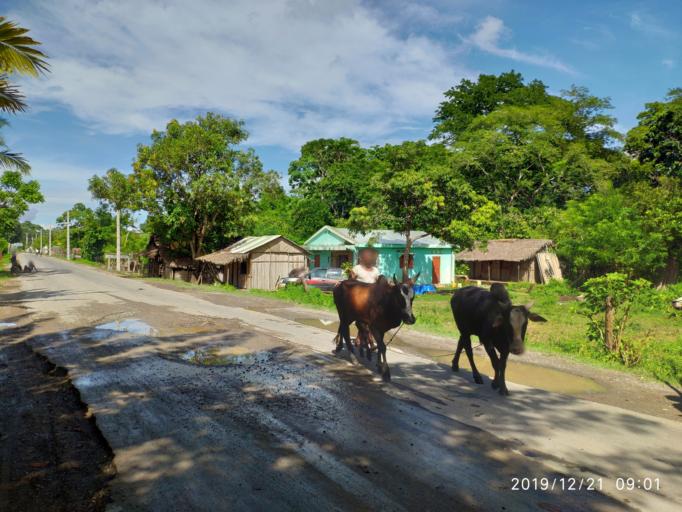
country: MG
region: Diana
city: Ambanja
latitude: -13.6301
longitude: 48.4553
